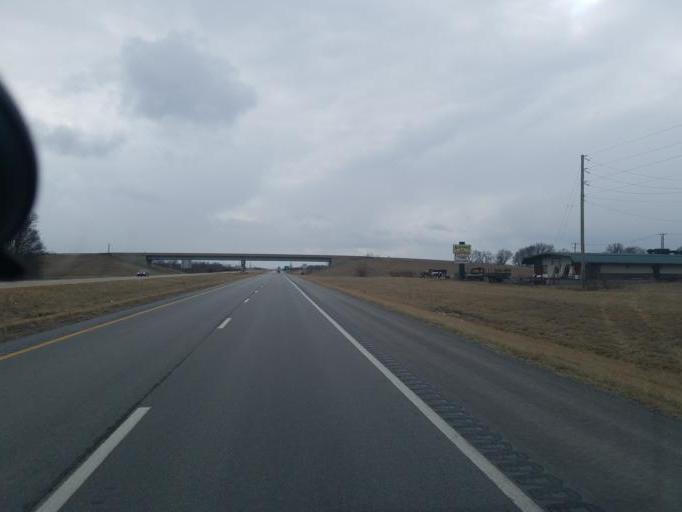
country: US
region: Missouri
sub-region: Randolph County
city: Moberly
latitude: 39.4106
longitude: -92.4125
